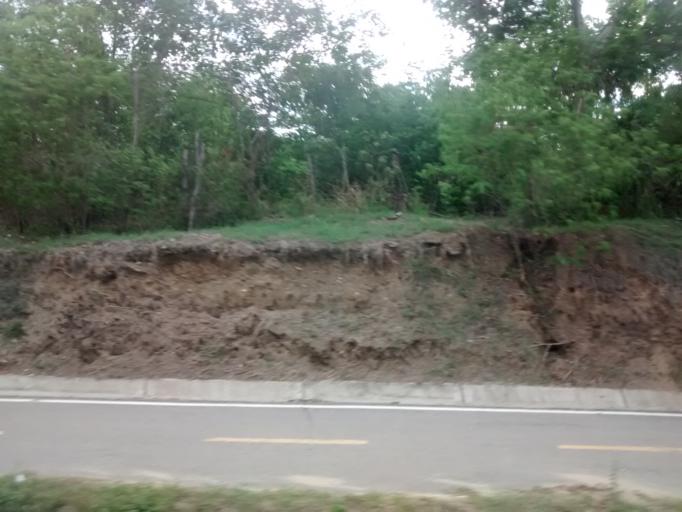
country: CO
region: Cundinamarca
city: Ricaurte
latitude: 4.2741
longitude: -74.7570
